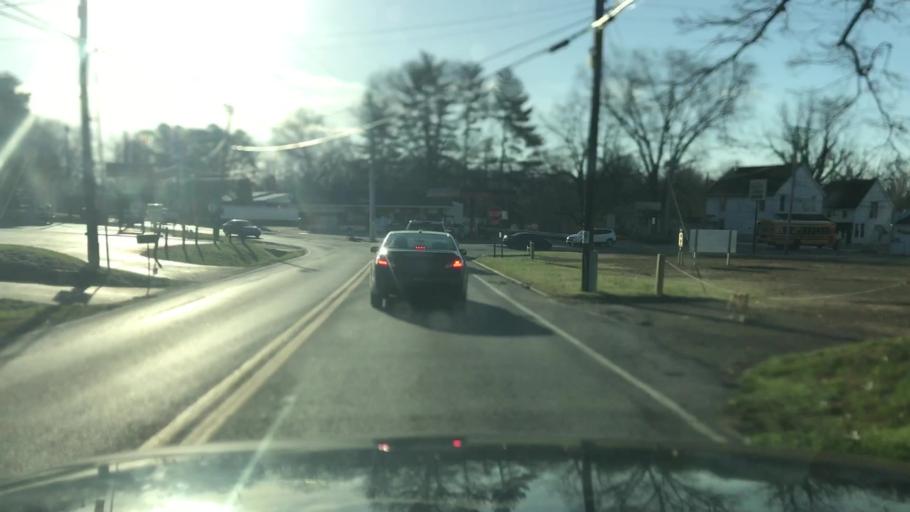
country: US
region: Indiana
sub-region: Vanderburgh County
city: Highland
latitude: 38.0341
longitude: -87.5628
